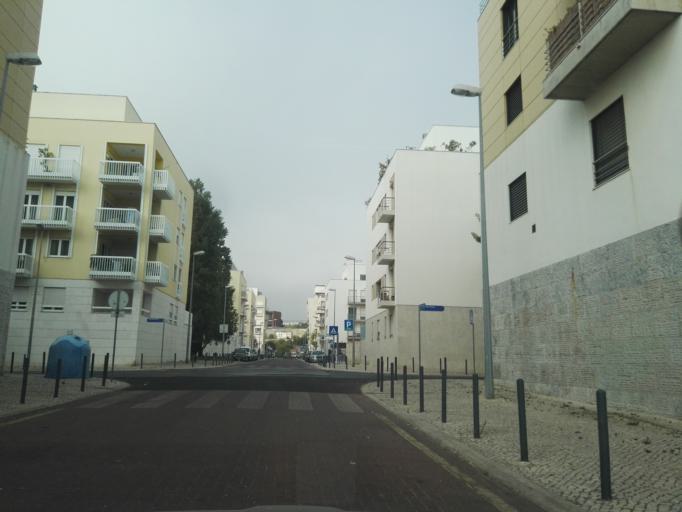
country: PT
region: Lisbon
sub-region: Loures
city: Moscavide
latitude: 38.7595
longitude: -9.0937
